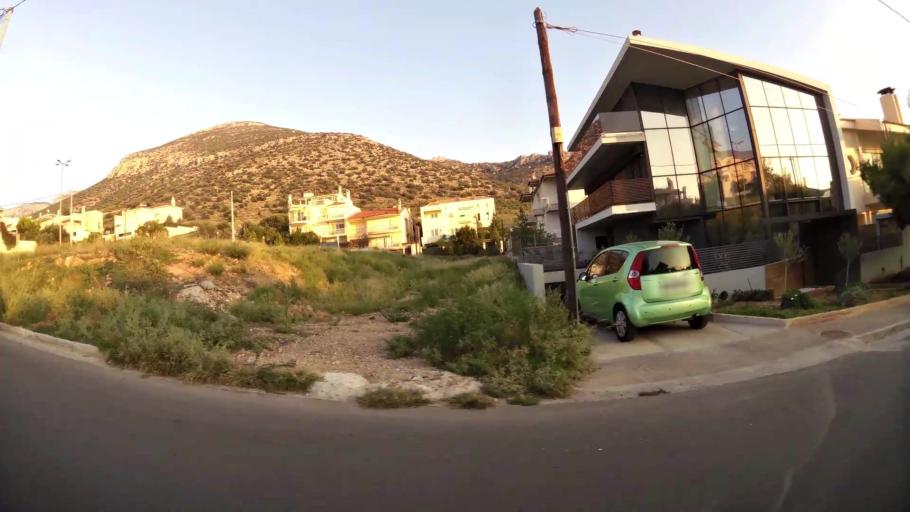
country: GR
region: Attica
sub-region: Nomarchia Athinas
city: Glyfada
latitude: 37.8828
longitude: 23.7723
